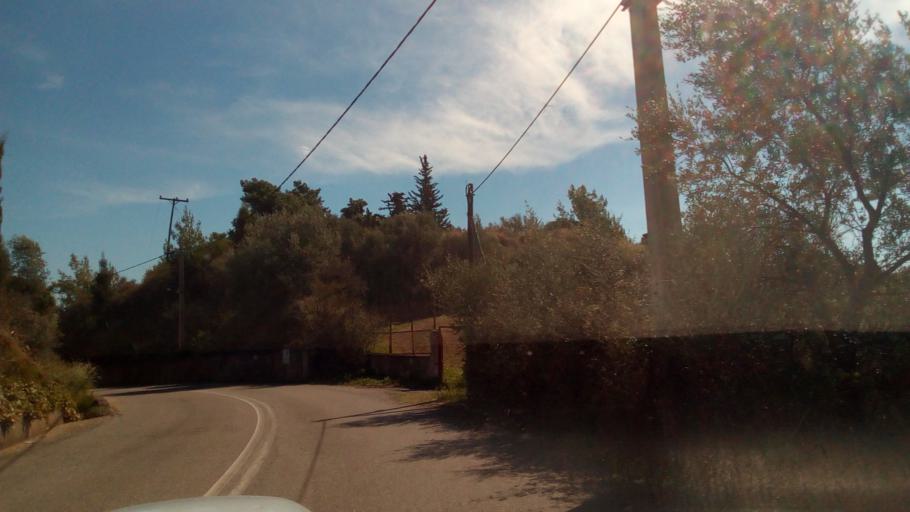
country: GR
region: West Greece
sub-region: Nomos Aitolias kai Akarnanias
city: Antirrio
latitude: 38.3682
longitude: 21.7771
